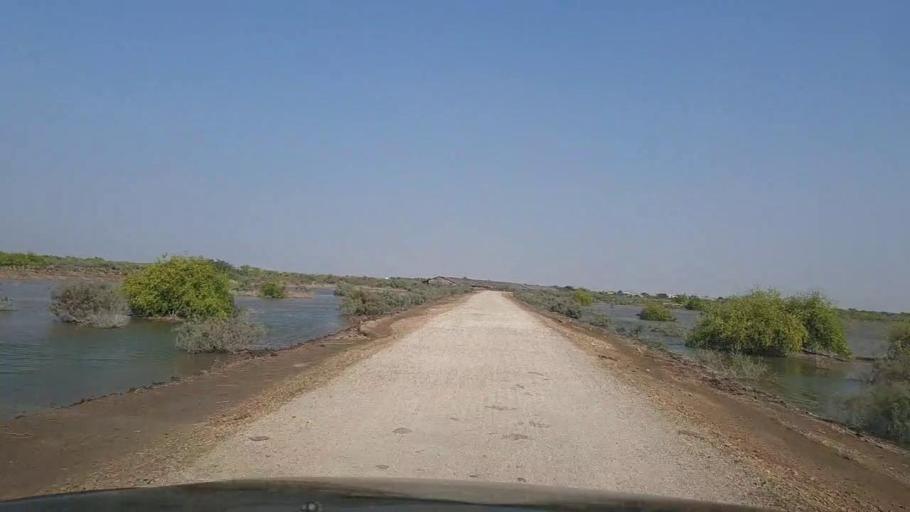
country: PK
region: Sindh
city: Thatta
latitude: 24.6433
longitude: 67.8155
